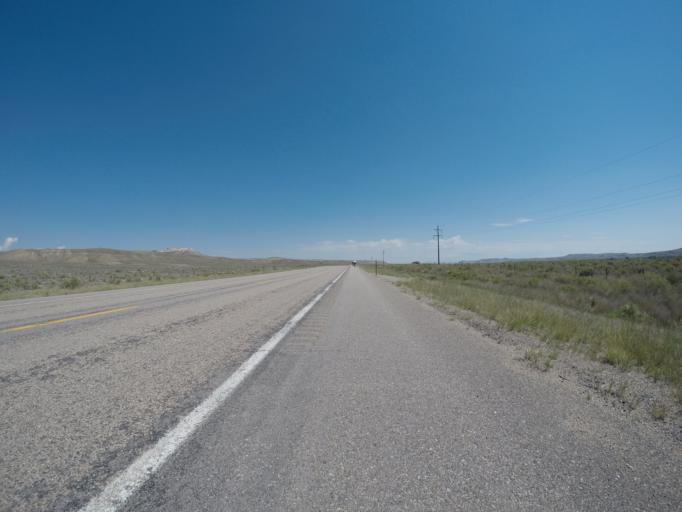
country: US
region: Wyoming
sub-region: Sublette County
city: Marbleton
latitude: 42.3618
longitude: -110.1539
